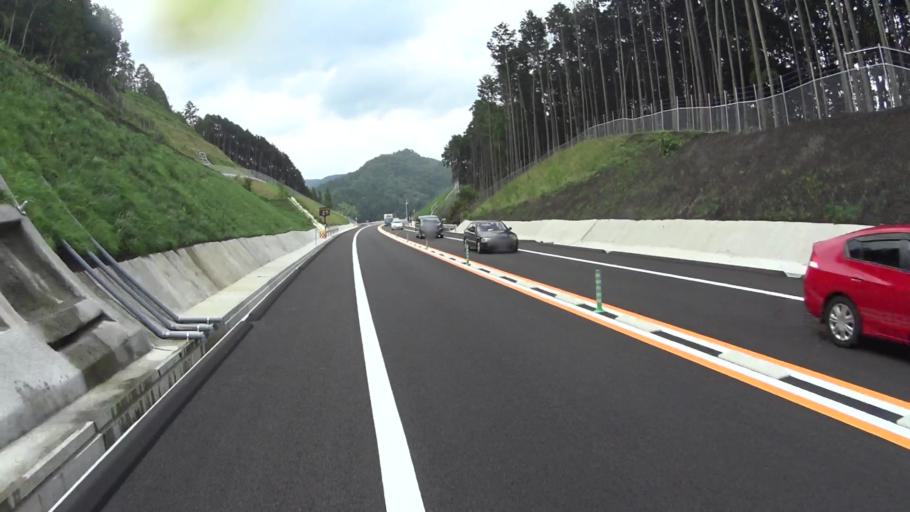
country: JP
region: Kyoto
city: Ayabe
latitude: 35.2139
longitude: 135.3435
